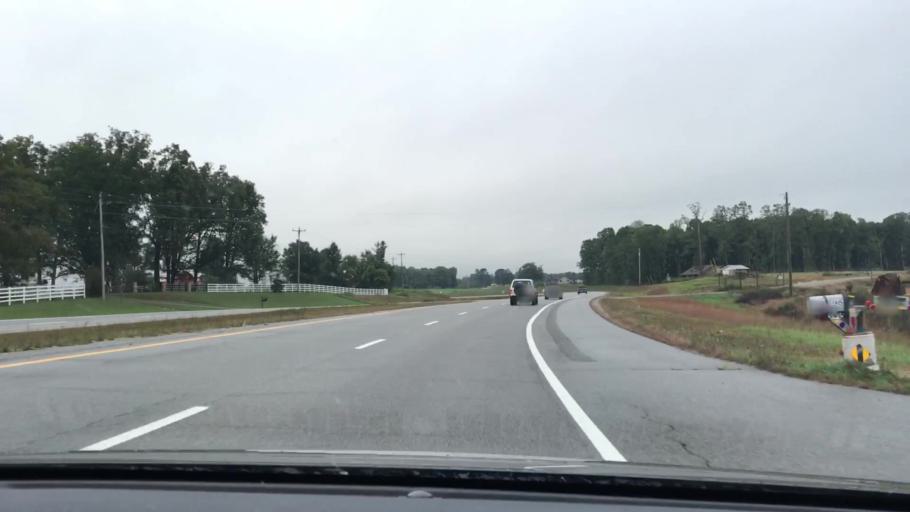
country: US
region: Tennessee
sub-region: Fentress County
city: Grimsley
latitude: 36.3166
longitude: -84.9684
